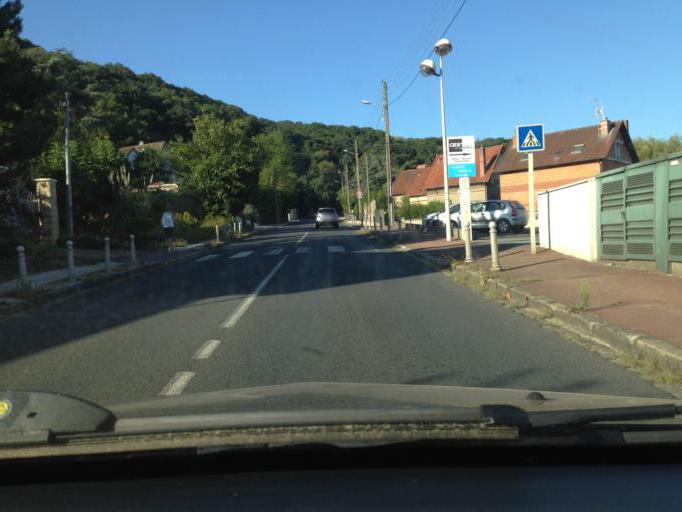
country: FR
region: Ile-de-France
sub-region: Departement des Yvelines
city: Saint-Remy-les-Chevreuse
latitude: 48.7072
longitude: 2.0752
